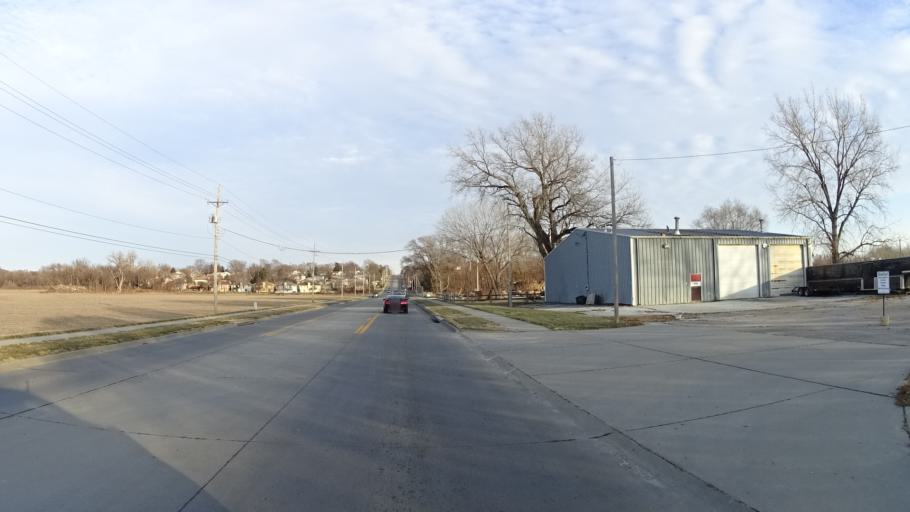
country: US
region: Nebraska
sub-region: Sarpy County
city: La Vista
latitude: 41.1907
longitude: -96.0046
